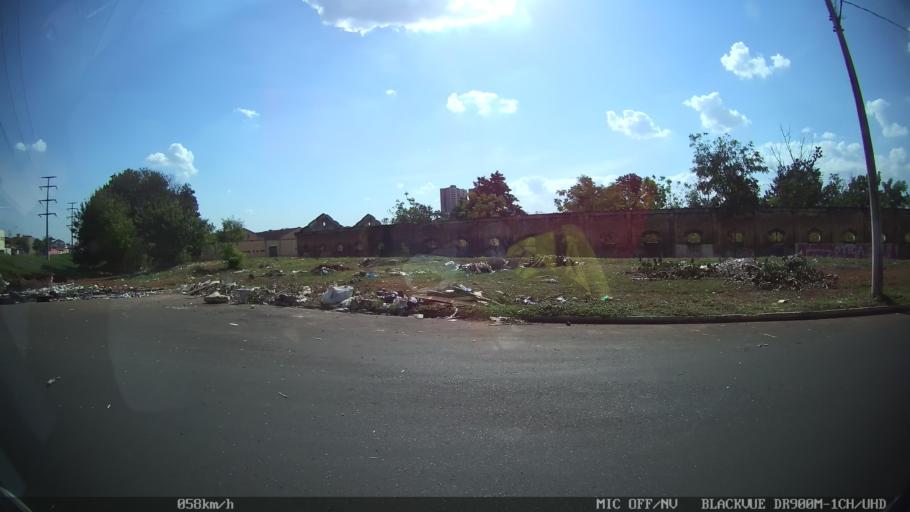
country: BR
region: Sao Paulo
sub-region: Ribeirao Preto
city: Ribeirao Preto
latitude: -21.1796
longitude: -47.8267
